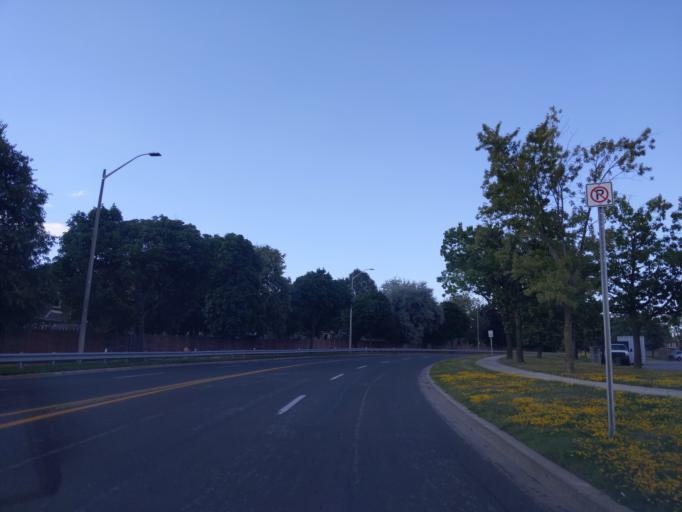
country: CA
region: Ontario
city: Markham
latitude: 43.8684
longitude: -79.2929
